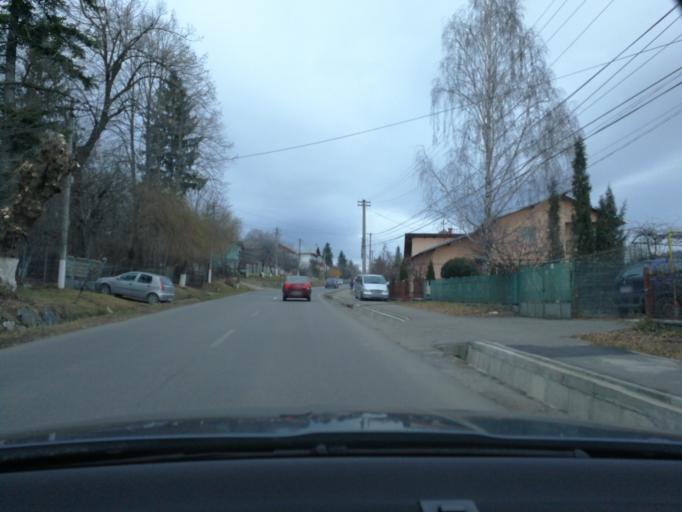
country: RO
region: Prahova
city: Cornu de Sus
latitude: 45.1576
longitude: 25.6872
